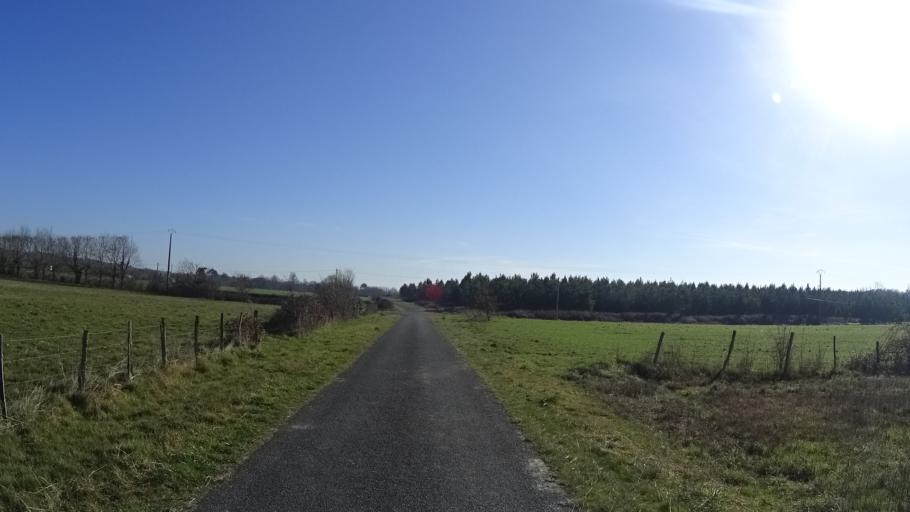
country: FR
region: Aquitaine
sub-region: Departement de la Dordogne
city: Montpon-Menesterol
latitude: 45.0335
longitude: 0.2308
